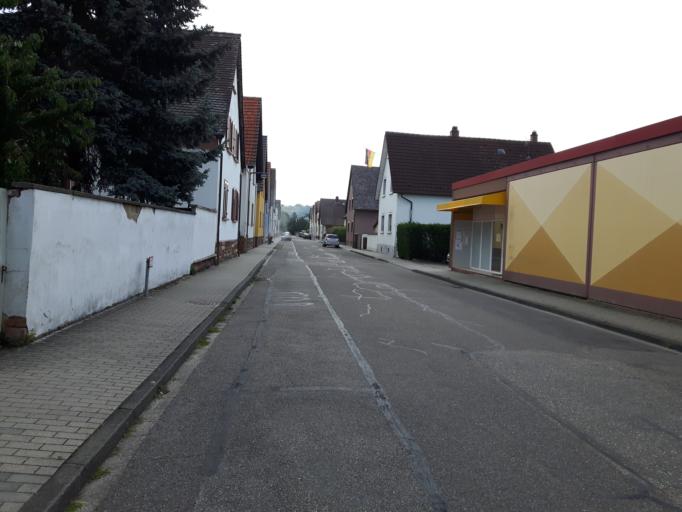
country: DE
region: Baden-Wuerttemberg
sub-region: Karlsruhe Region
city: Karlsdorf-Neuthard
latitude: 49.1013
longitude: 8.5290
